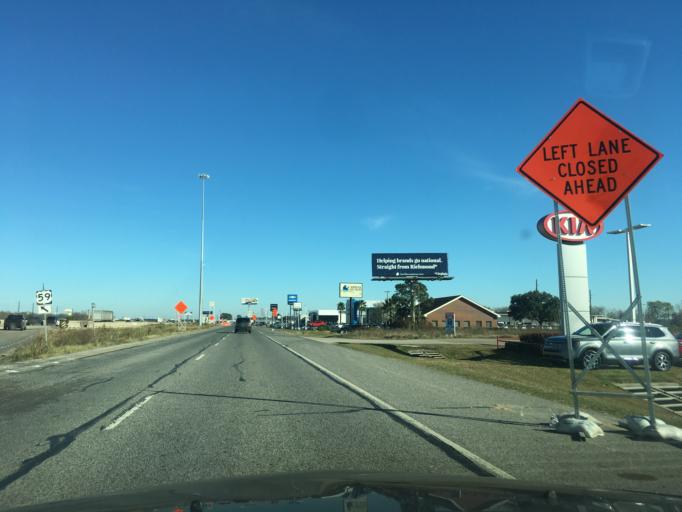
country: US
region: Texas
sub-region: Fort Bend County
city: Rosenberg
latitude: 29.5324
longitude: -95.7871
